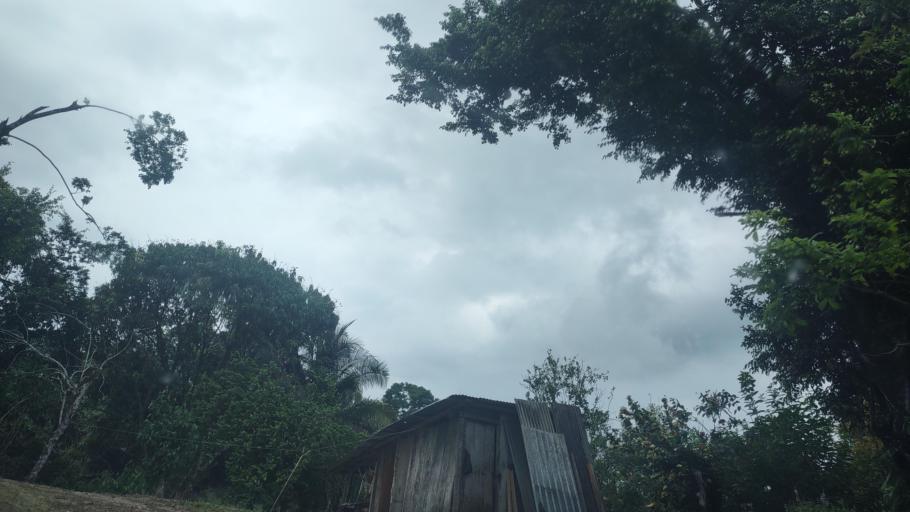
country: MX
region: Veracruz
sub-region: Uxpanapa
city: Poblado 10
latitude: 17.4517
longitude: -94.0993
